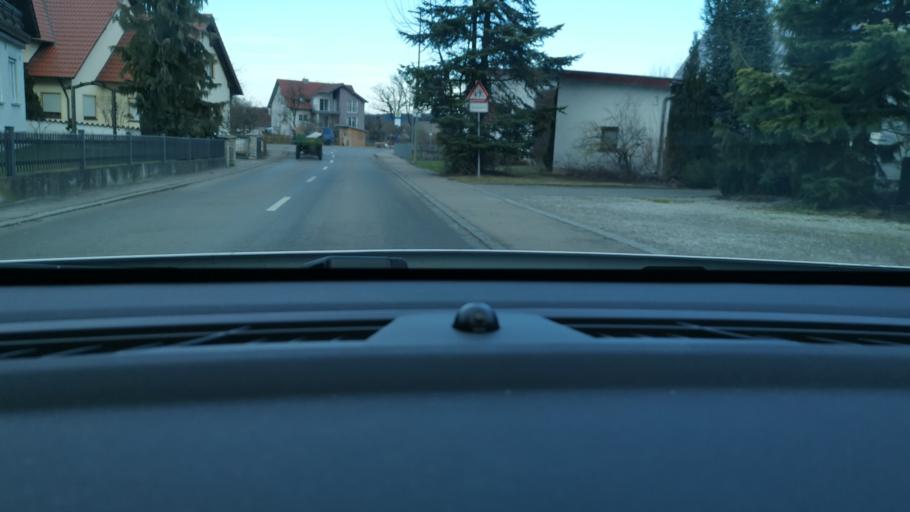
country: DE
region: Bavaria
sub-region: Swabia
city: Affing
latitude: 48.4944
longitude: 10.9820
